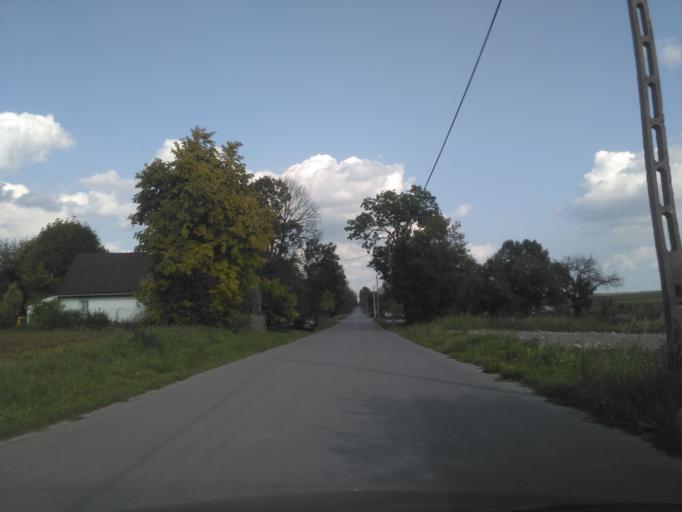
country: PL
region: Lublin Voivodeship
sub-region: Powiat chelmski
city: Pokrowka
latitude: 51.0676
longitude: 23.4836
